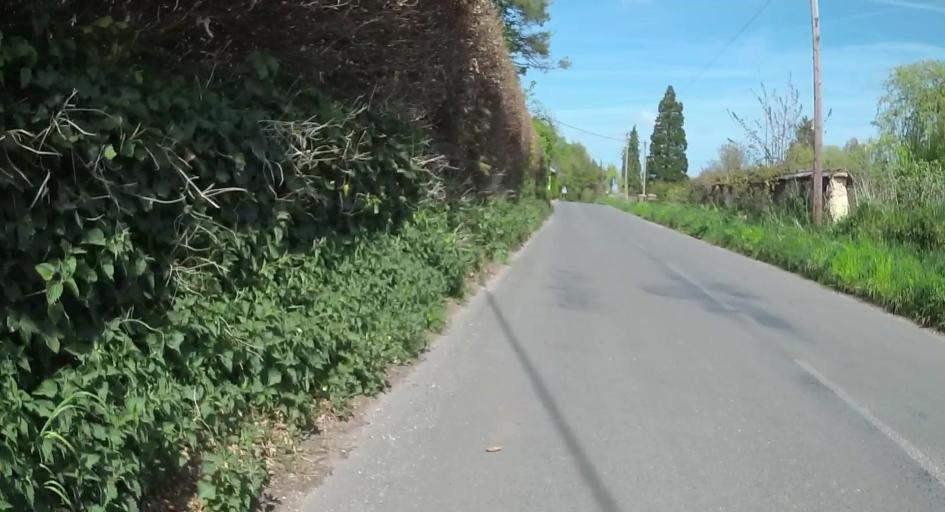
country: GB
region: England
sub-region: Hampshire
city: Abbotts Ann
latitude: 51.1157
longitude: -1.4982
